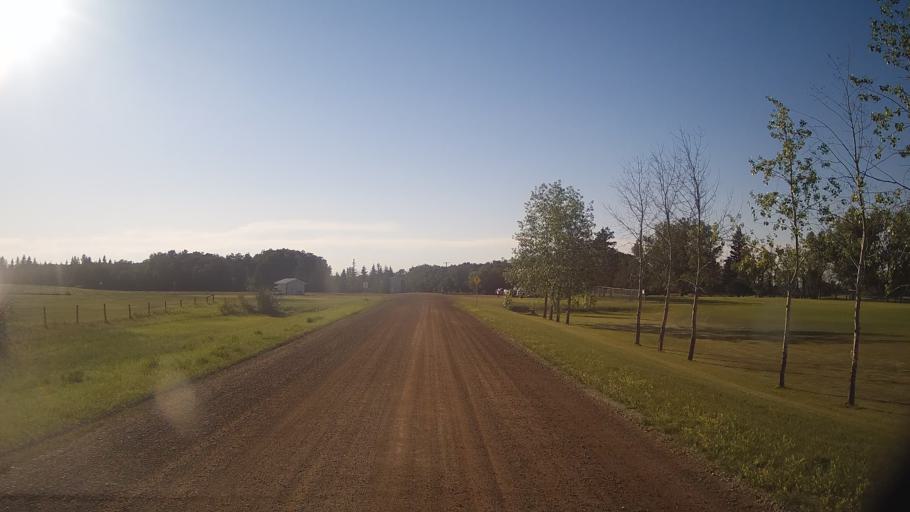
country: CA
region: Saskatchewan
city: Lanigan
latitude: 51.8501
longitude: -105.0160
